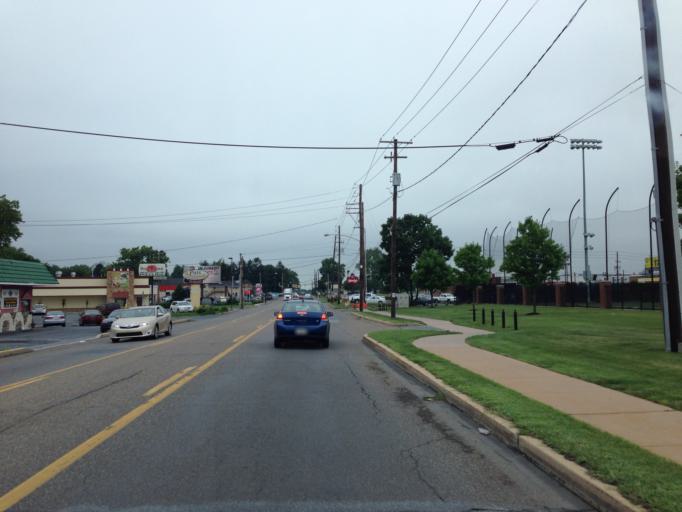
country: US
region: Pennsylvania
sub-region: Lancaster County
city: Lancaster
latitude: 40.0521
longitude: -76.3221
